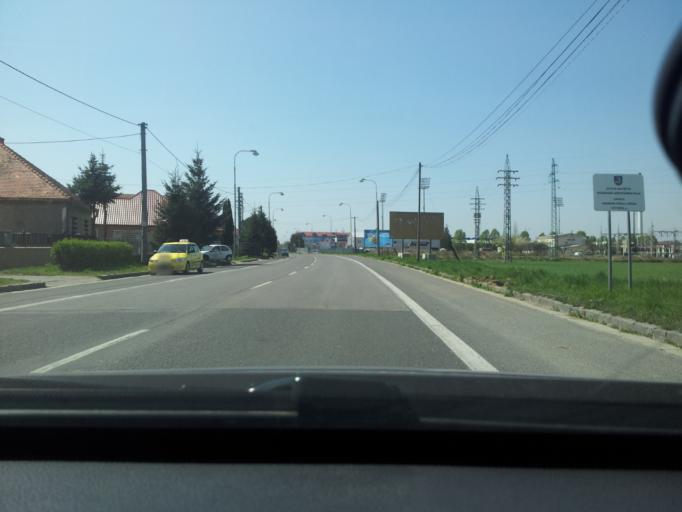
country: SK
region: Nitriansky
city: Zlate Moravce
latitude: 48.4008
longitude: 18.4087
